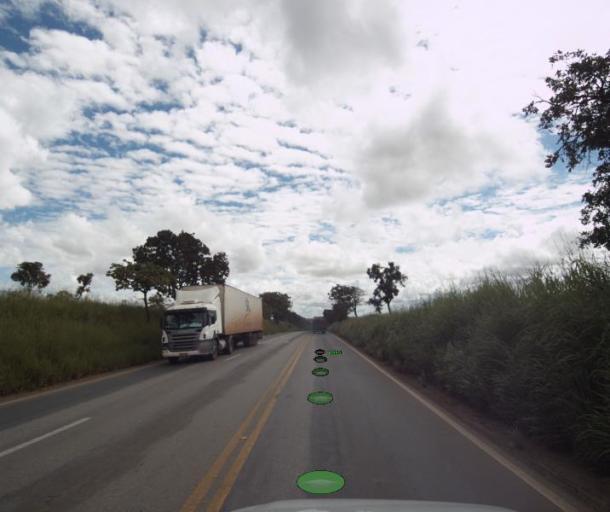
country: BR
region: Goias
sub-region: Uruacu
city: Uruacu
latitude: -14.3880
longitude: -49.1578
